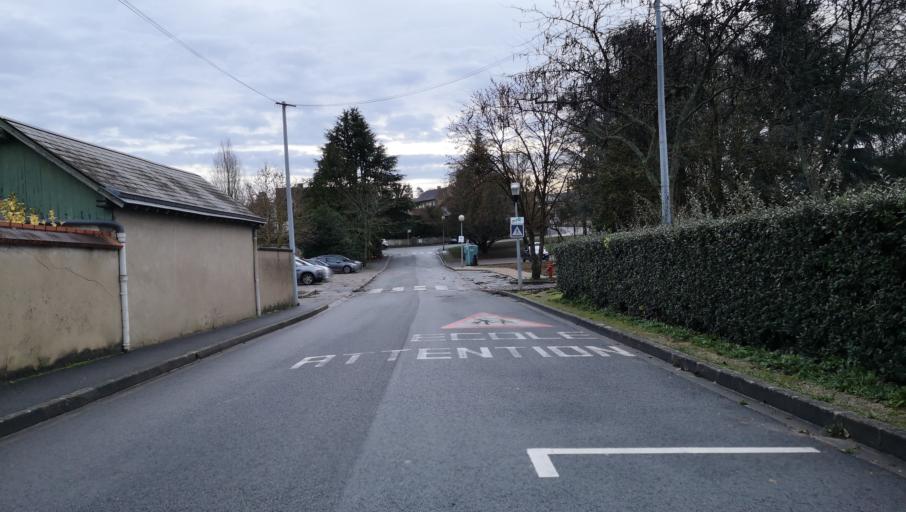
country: FR
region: Centre
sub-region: Departement du Loiret
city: Saint-Jean-de-Braye
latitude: 47.9060
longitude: 1.9641
